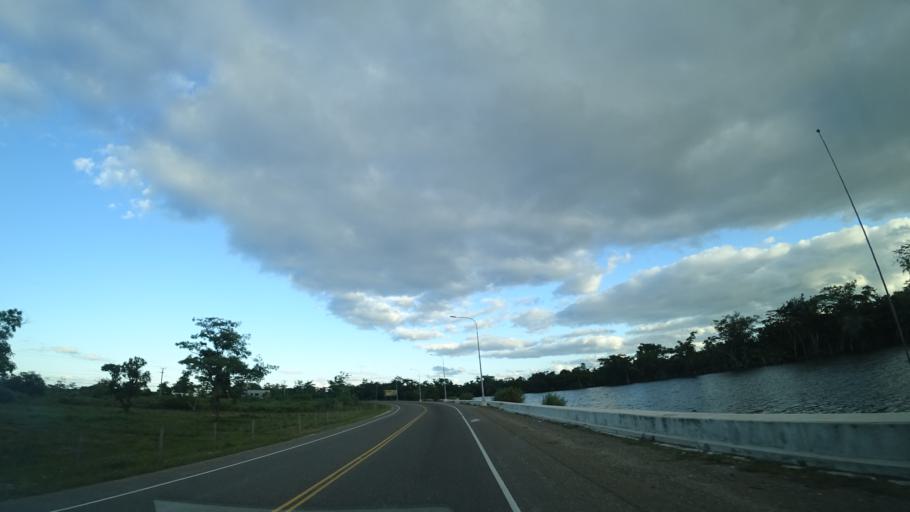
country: BZ
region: Belize
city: Belize City
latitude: 17.5428
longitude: -88.2638
